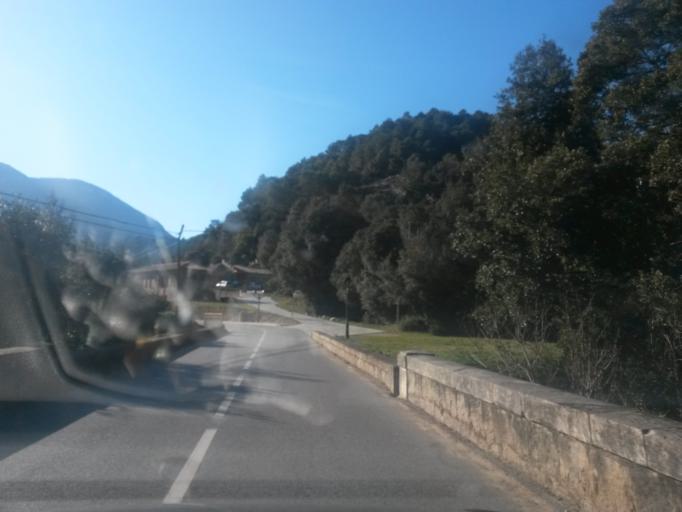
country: ES
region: Catalonia
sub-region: Provincia de Girona
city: Sant Llorenc de la Muga
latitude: 42.3060
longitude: 2.7227
